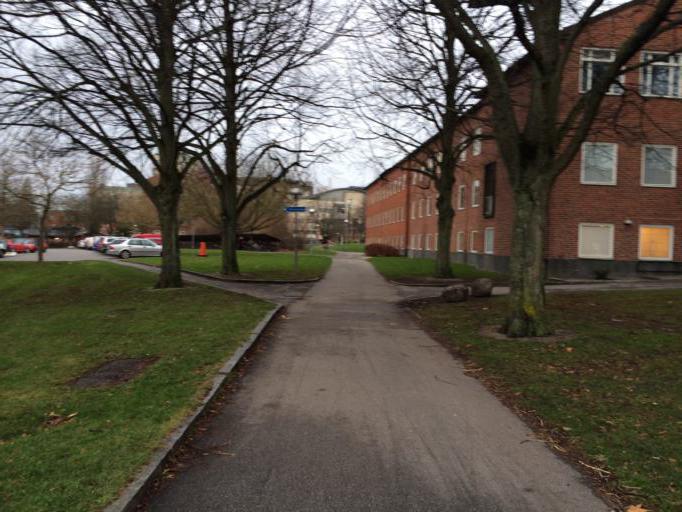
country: SE
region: Skane
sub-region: Lunds Kommun
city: Lund
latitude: 55.7100
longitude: 13.2038
